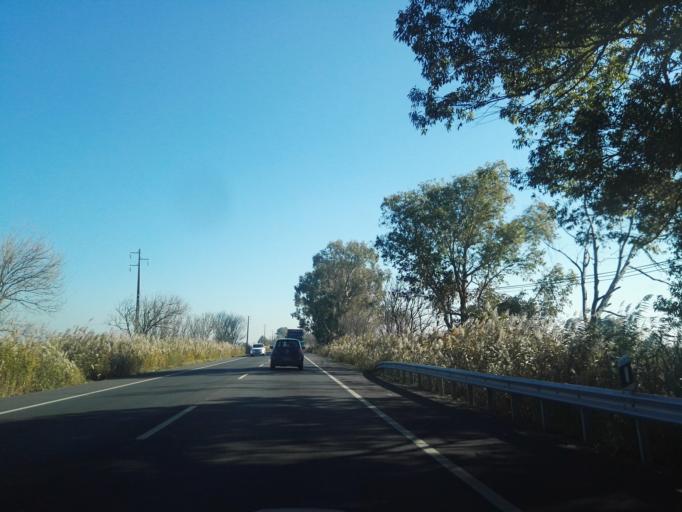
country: PT
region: Lisbon
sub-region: Vila Franca de Xira
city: Vila Franca de Xira
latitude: 38.9493
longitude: -8.9673
